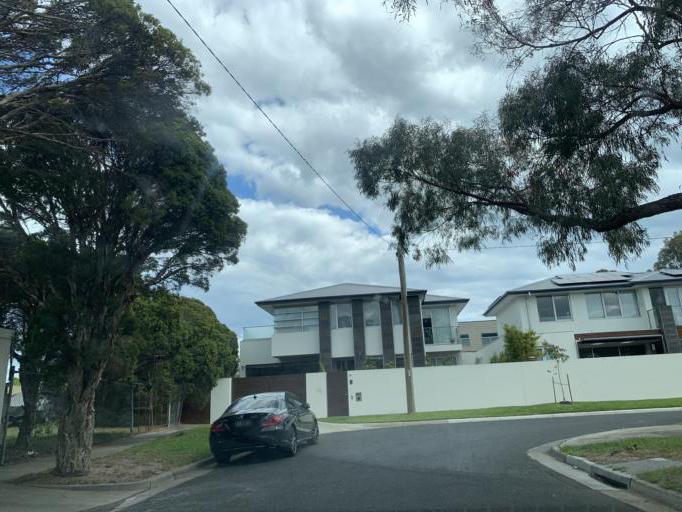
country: AU
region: Victoria
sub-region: Bayside
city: Hampton
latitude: -37.9368
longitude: 145.0142
